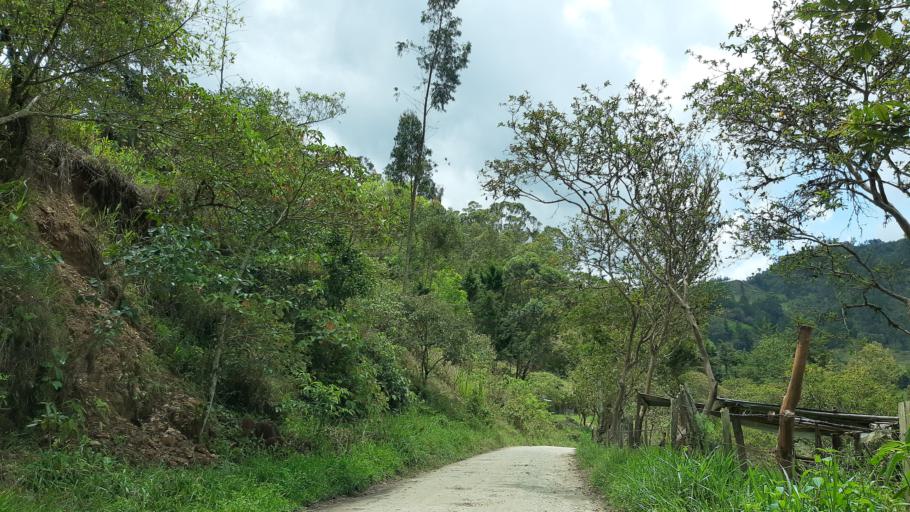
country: CO
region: Boyaca
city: Garagoa
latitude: 5.0722
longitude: -73.3635
